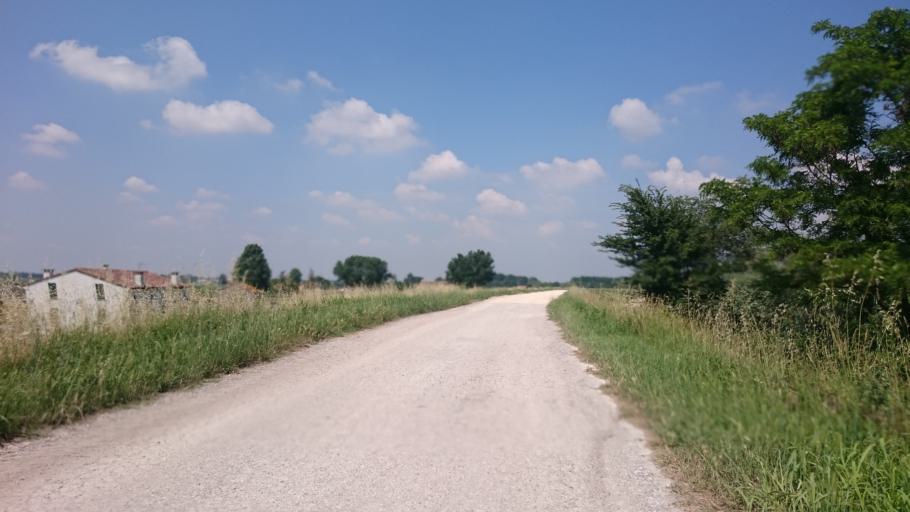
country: IT
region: Lombardy
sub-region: Provincia di Mantova
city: San Benedetto Po
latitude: 45.0918
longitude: 10.9339
